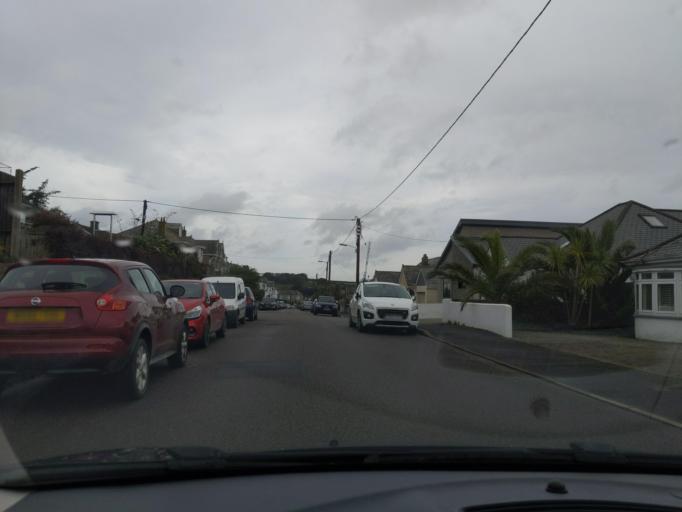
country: GB
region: England
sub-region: Cornwall
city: Padstow
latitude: 50.5365
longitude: -4.9368
